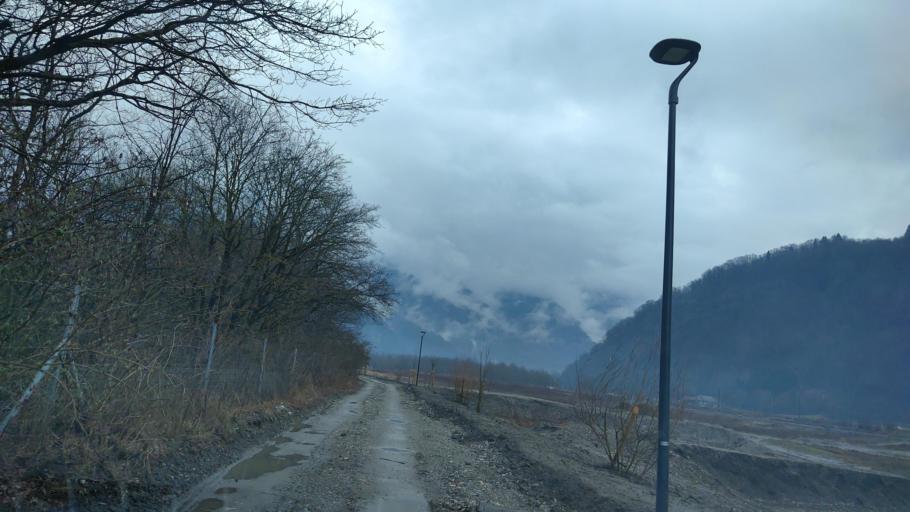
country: FR
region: Rhone-Alpes
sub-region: Departement de la Savoie
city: Aiton
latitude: 45.5562
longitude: 6.2726
